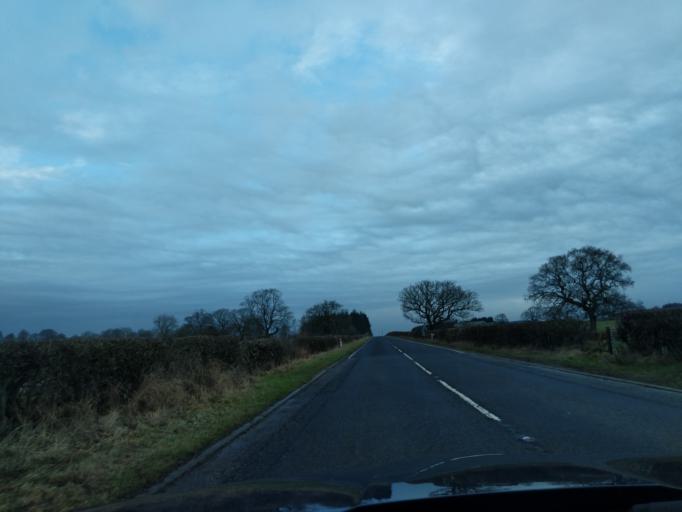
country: GB
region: England
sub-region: Northumberland
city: Rothley
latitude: 55.1237
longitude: -1.9248
